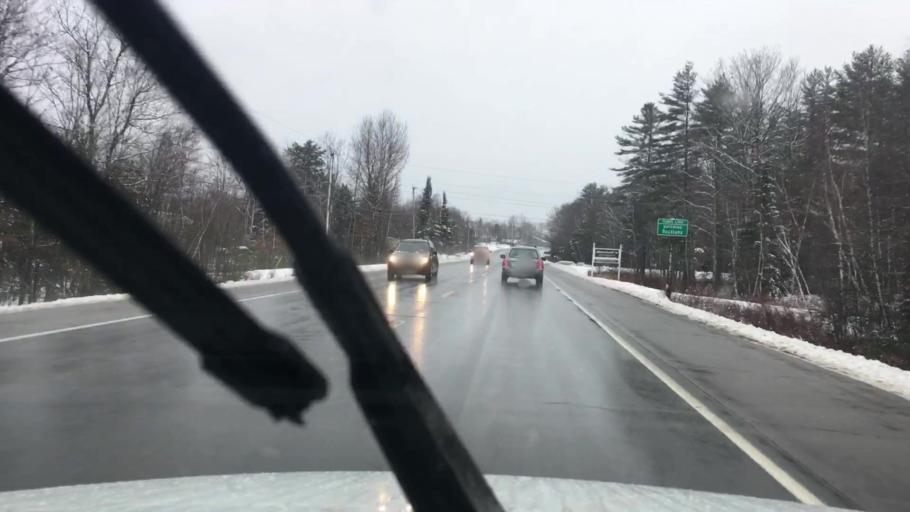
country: US
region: Maine
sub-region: Knox County
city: Rockport
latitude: 44.1698
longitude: -69.1557
